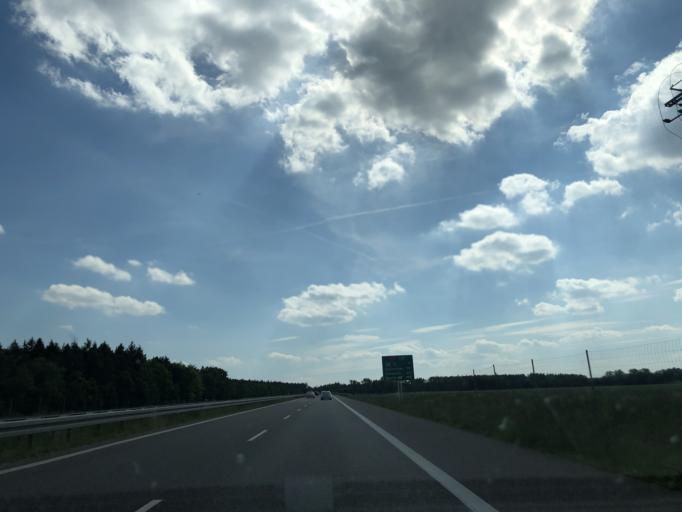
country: PL
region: West Pomeranian Voivodeship
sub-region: Powiat goleniowski
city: Nowogard
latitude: 53.6786
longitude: 15.0838
